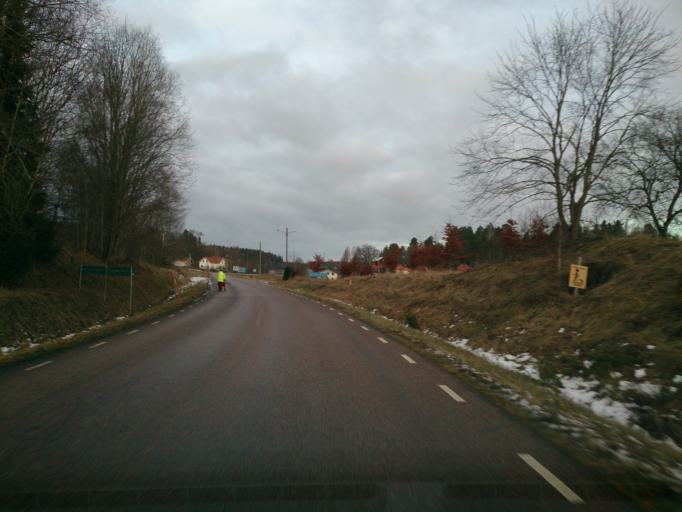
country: SE
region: OEstergoetland
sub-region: Atvidabergs Kommun
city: Atvidaberg
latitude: 58.3341
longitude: 16.0281
